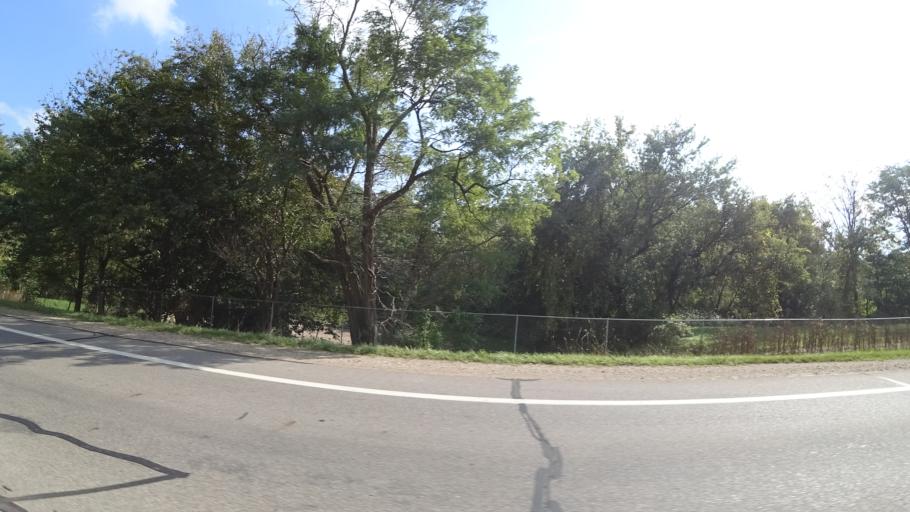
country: US
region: Michigan
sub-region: Saint Joseph County
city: Colon
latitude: 42.0079
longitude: -85.4286
